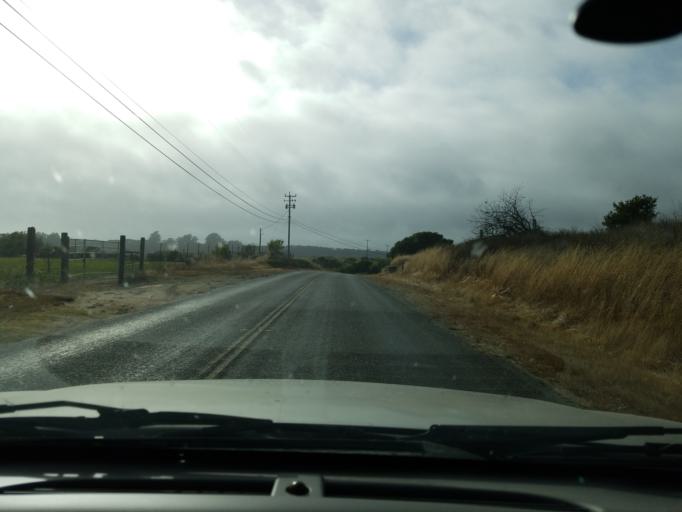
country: US
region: California
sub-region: Monterey County
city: Elkhorn
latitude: 36.8453
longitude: -121.7478
